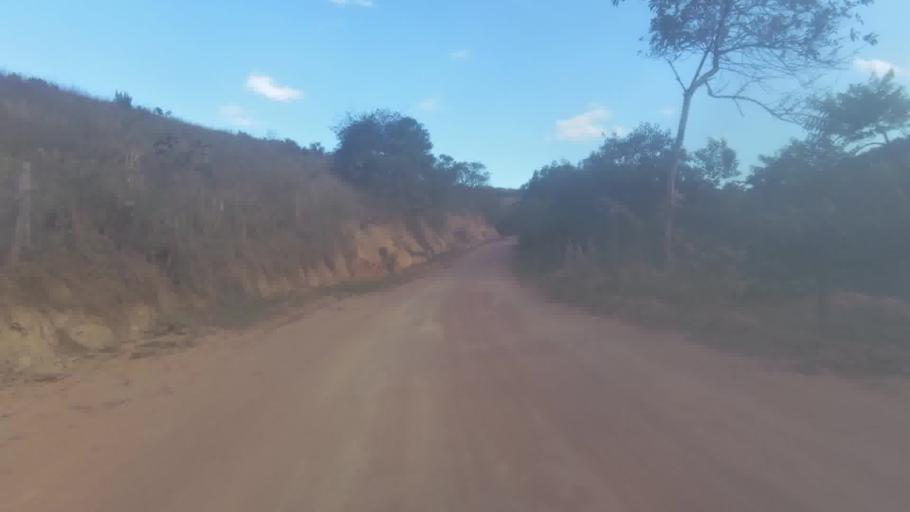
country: BR
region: Espirito Santo
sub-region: Mimoso Do Sul
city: Mimoso do Sul
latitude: -21.0849
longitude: -41.1458
